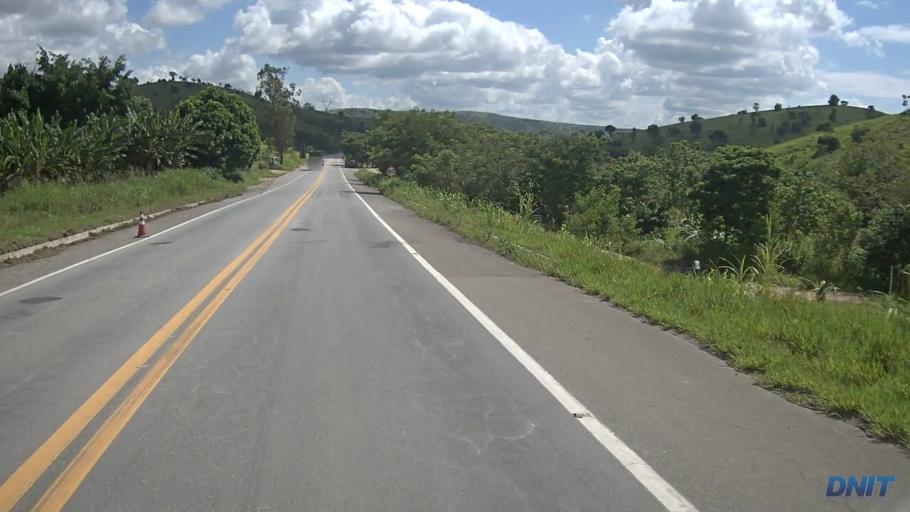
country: BR
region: Minas Gerais
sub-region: Governador Valadares
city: Governador Valadares
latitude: -19.0197
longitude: -42.1424
